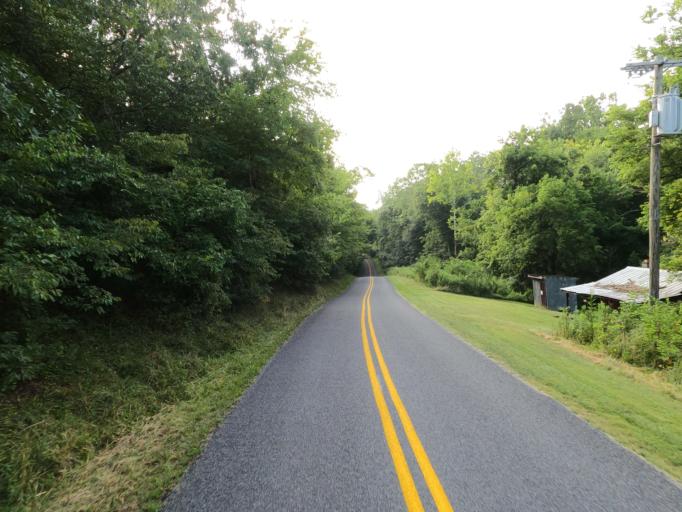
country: US
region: West Virginia
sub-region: Morgan County
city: Berkeley Springs
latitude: 39.6361
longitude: -78.3209
